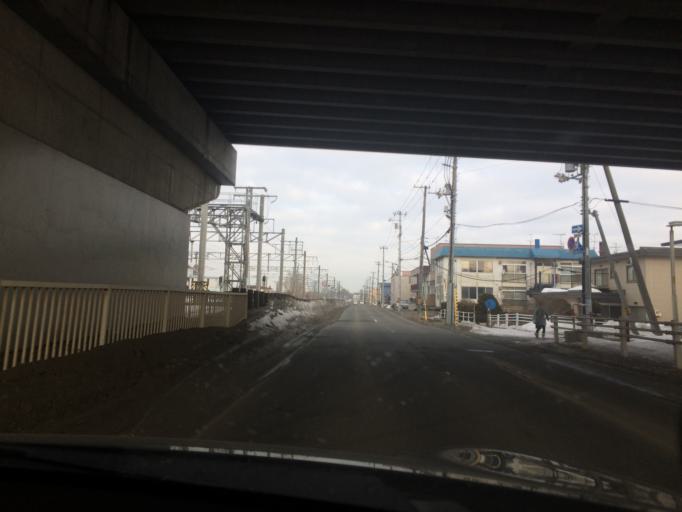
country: JP
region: Hokkaido
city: Sapporo
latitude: 43.0618
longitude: 141.4026
